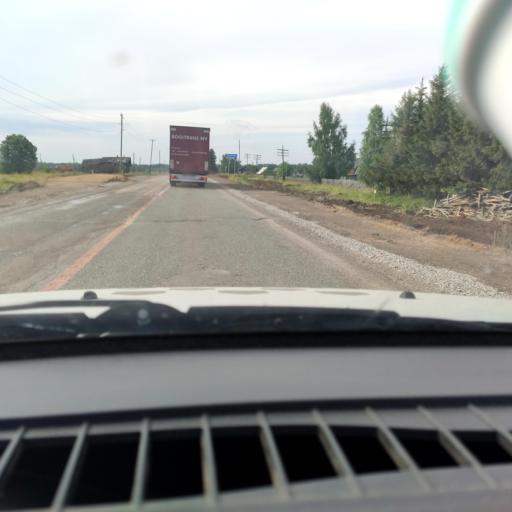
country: RU
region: Kirov
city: Kostino
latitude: 58.8332
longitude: 53.3067
